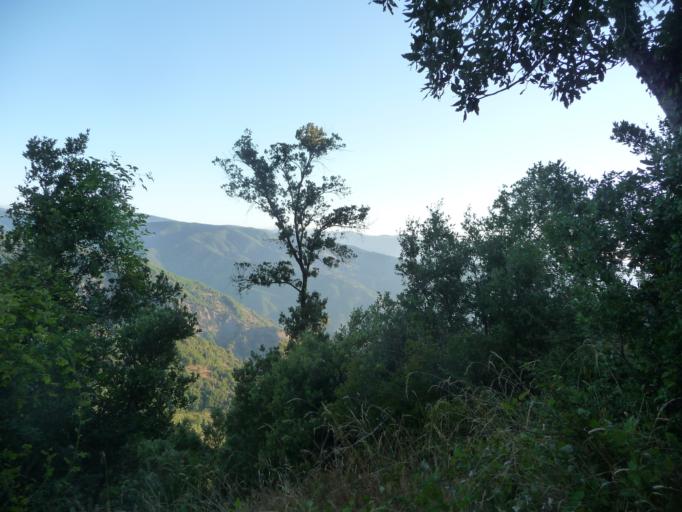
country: IT
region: Calabria
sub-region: Provincia di Reggio Calabria
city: Pazzano
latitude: 38.4630
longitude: 16.4282
